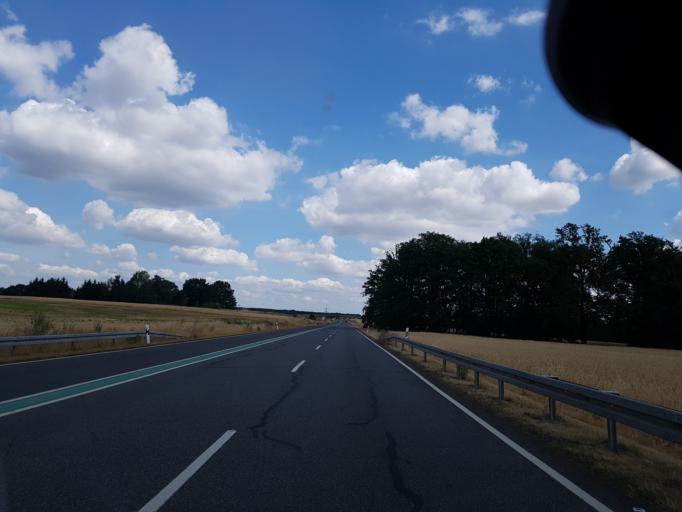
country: DE
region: Brandenburg
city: Drebkau
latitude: 51.6466
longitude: 14.2388
